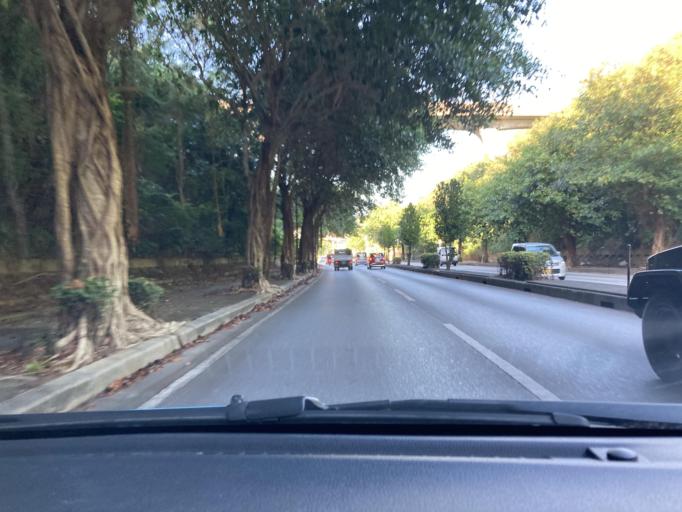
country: JP
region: Okinawa
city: Tomigusuku
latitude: 26.1752
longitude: 127.7126
